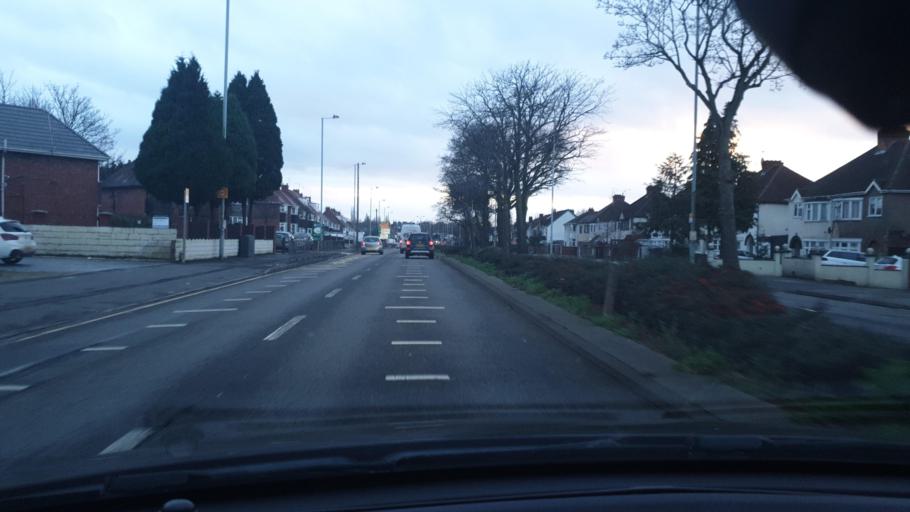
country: GB
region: England
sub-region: Wolverhampton
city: Wolverhampton
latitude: 52.6239
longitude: -2.1282
